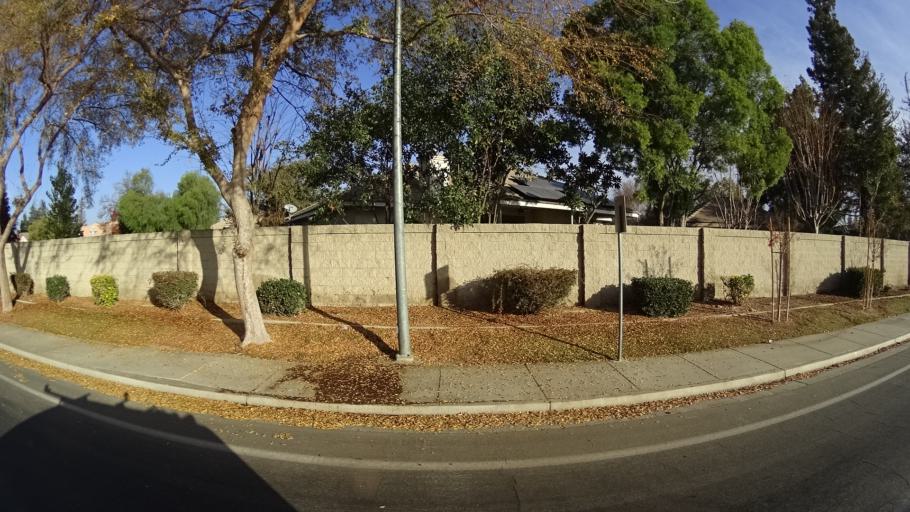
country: US
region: California
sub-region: Kern County
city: Greenacres
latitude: 35.4017
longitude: -119.0678
